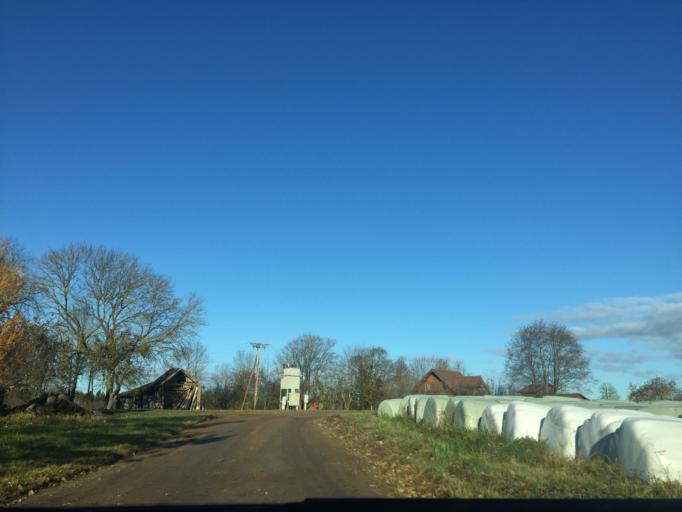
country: LV
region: Engure
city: Smarde
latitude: 56.9330
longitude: 23.2887
